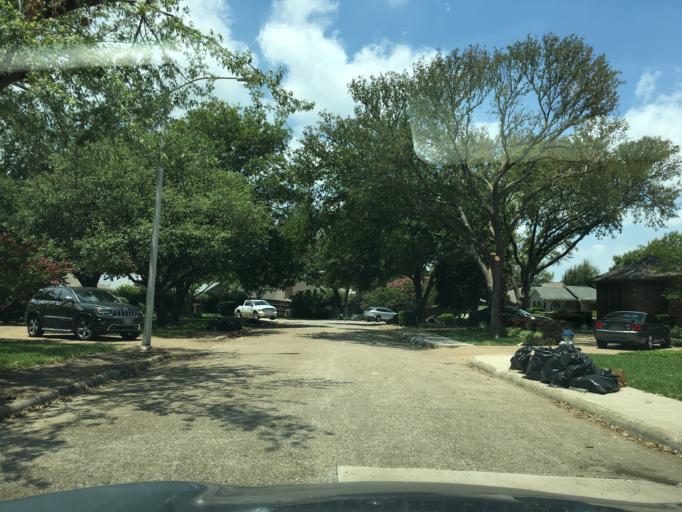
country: US
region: Texas
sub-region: Dallas County
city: Richardson
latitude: 32.9063
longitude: -96.7439
